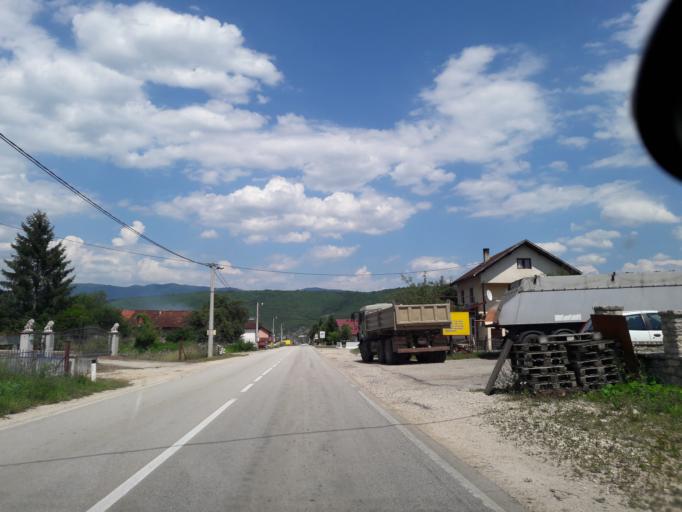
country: BA
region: Republika Srpska
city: Mrkonjic Grad
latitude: 44.4346
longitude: 17.1465
